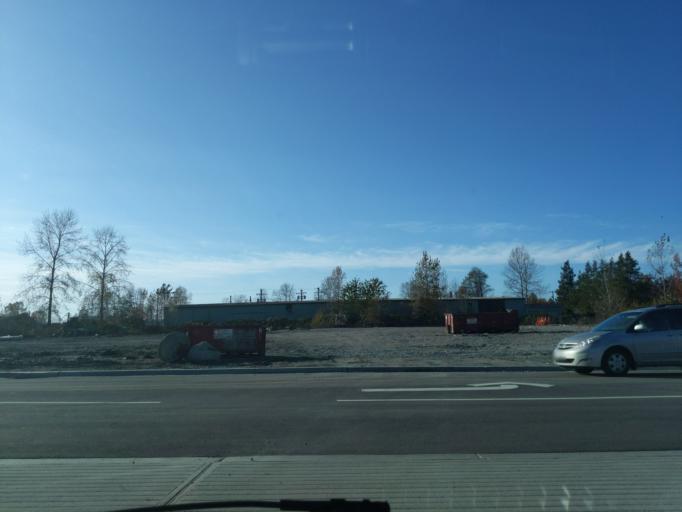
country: CA
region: British Columbia
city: New Westminster
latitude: 49.2021
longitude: -122.8721
